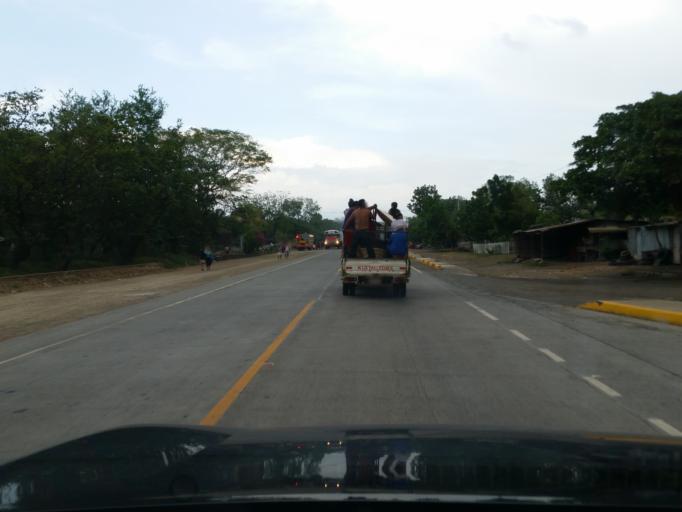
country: NI
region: Managua
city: Carlos Fonseca Amador
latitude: 12.0682
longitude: -86.4816
